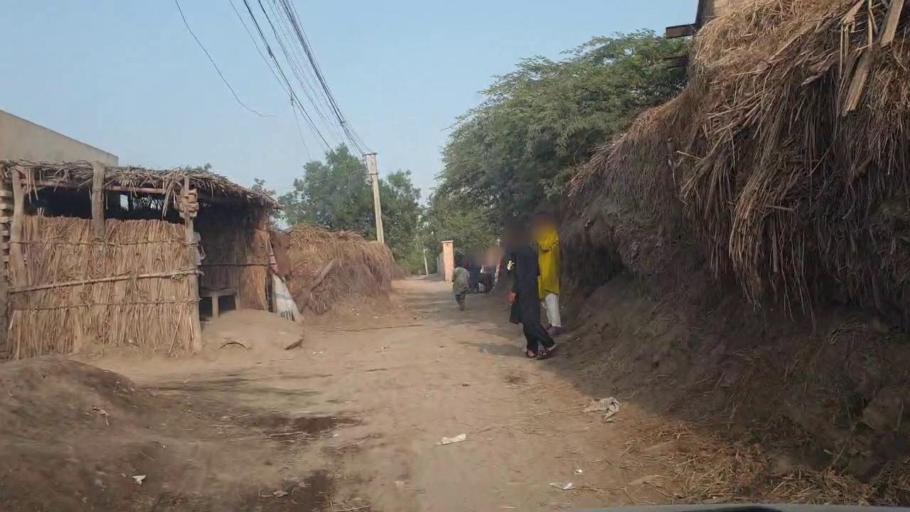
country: PK
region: Sindh
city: Matli
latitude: 25.0367
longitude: 68.7397
